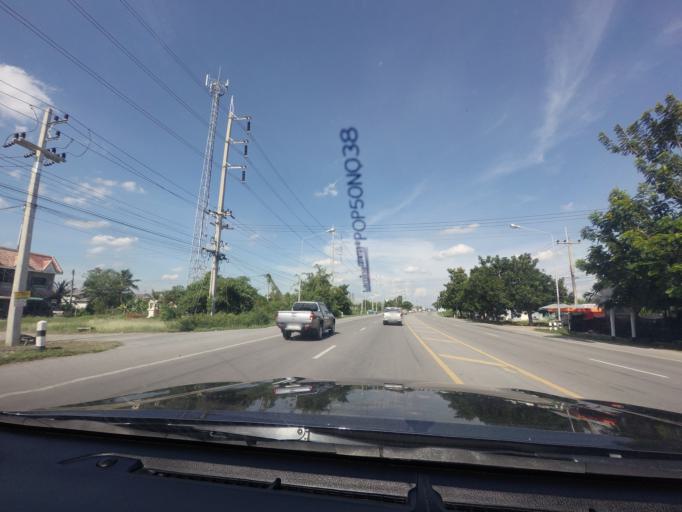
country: TH
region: Nakhon Pathom
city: Bang Len
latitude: 14.1575
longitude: 100.1645
